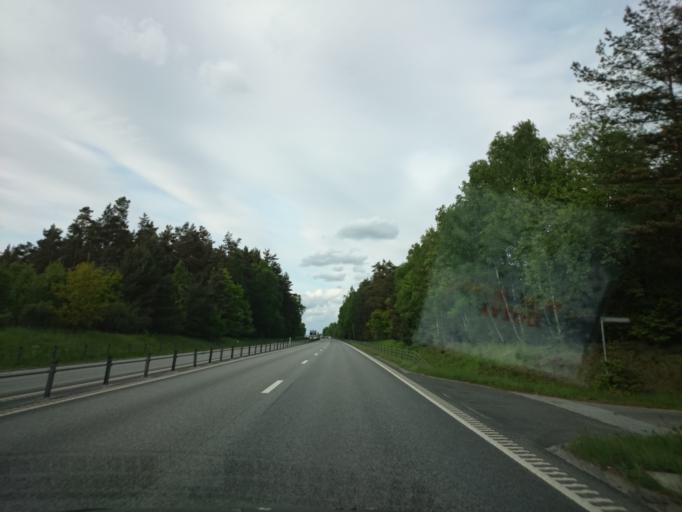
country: SE
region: Skane
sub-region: Kristianstads Kommun
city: Norra Asum
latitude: 55.9767
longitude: 14.0830
